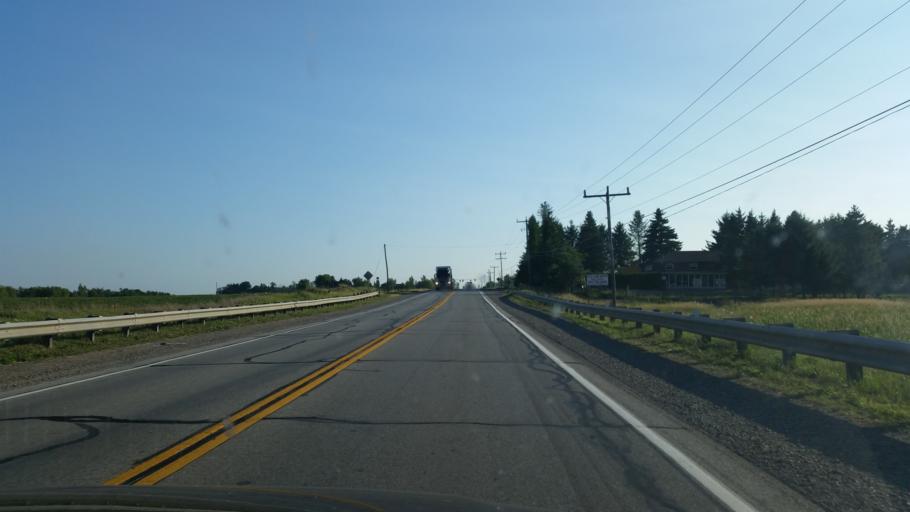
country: CA
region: Ontario
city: Brampton
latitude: 43.8249
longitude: -79.8225
